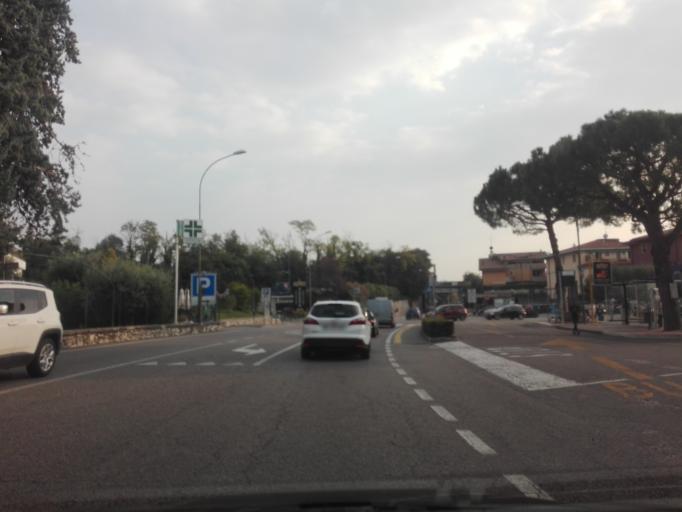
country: IT
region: Veneto
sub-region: Provincia di Verona
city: Bardolino
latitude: 45.5472
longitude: 10.7244
